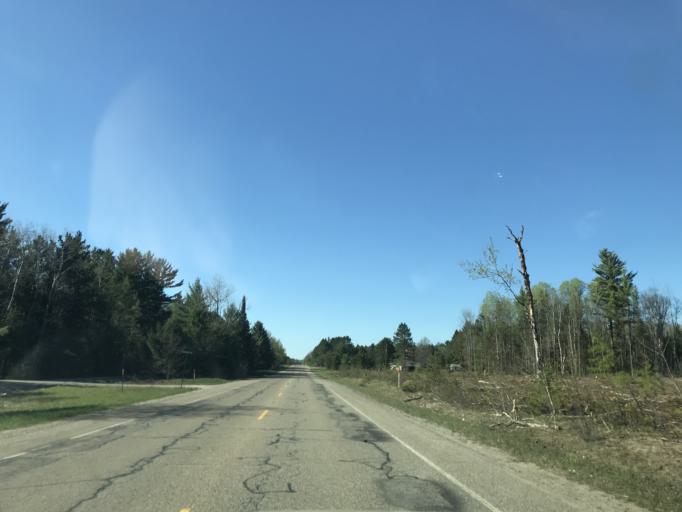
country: US
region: Michigan
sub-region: Crawford County
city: Grayling
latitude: 44.7407
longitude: -84.7503
